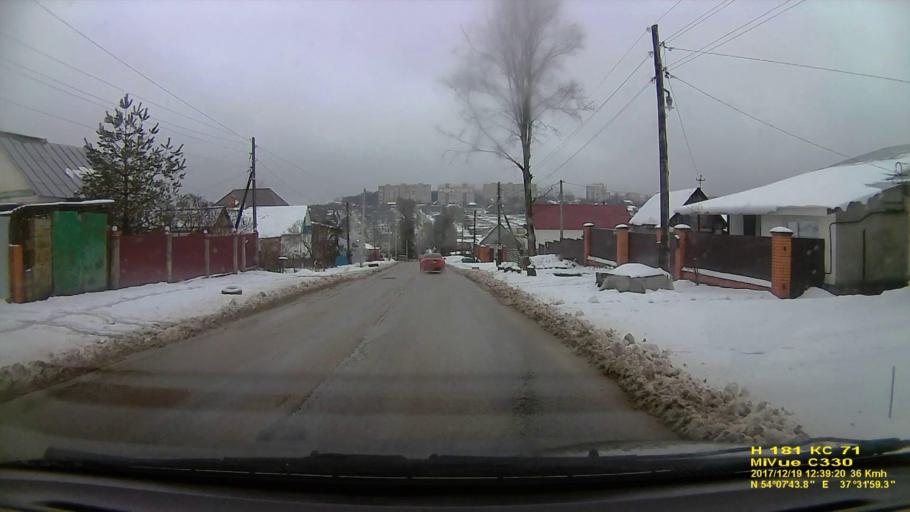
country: RU
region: Tula
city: Kosaya Gora
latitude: 54.1287
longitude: 37.5332
